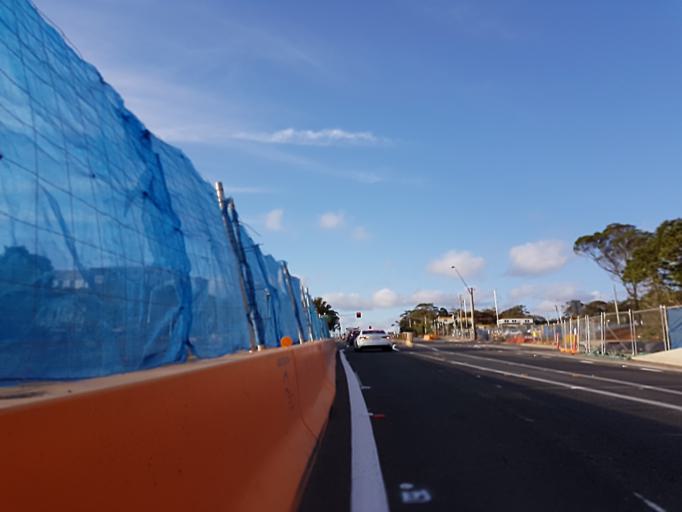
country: AU
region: New South Wales
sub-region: Warringah
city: Allambie Heights
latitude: -33.7537
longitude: 151.2341
